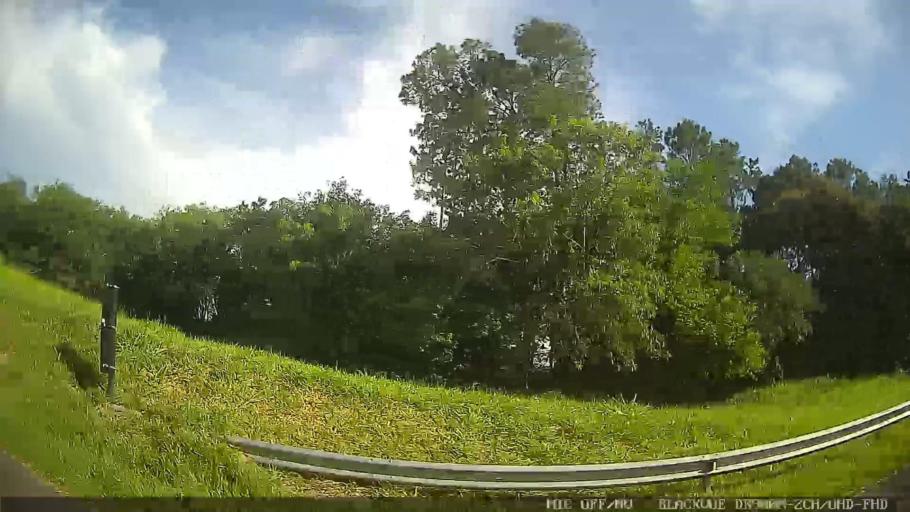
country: BR
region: Sao Paulo
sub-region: Tiete
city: Tiete
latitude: -23.1166
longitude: -47.7288
